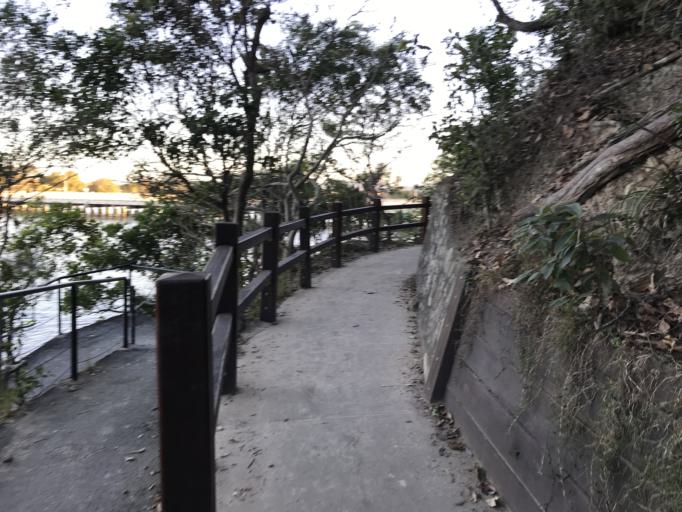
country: AU
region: Queensland
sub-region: Gold Coast
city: Palm Beach
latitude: -28.0971
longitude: 153.4568
